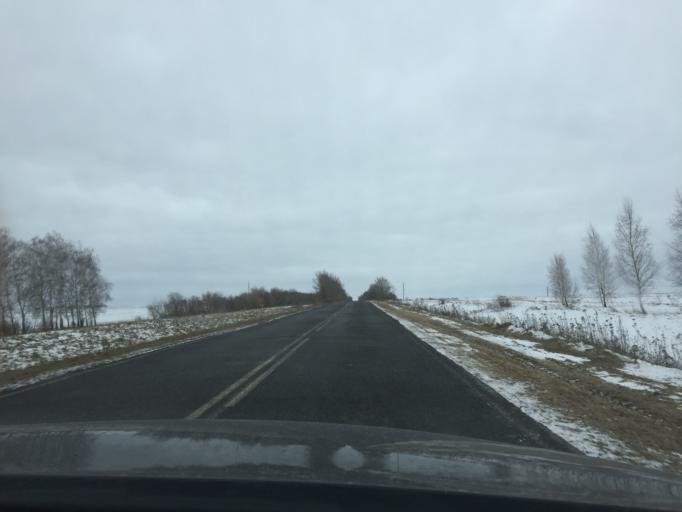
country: RU
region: Tula
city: Shchekino
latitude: 53.8261
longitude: 37.5173
